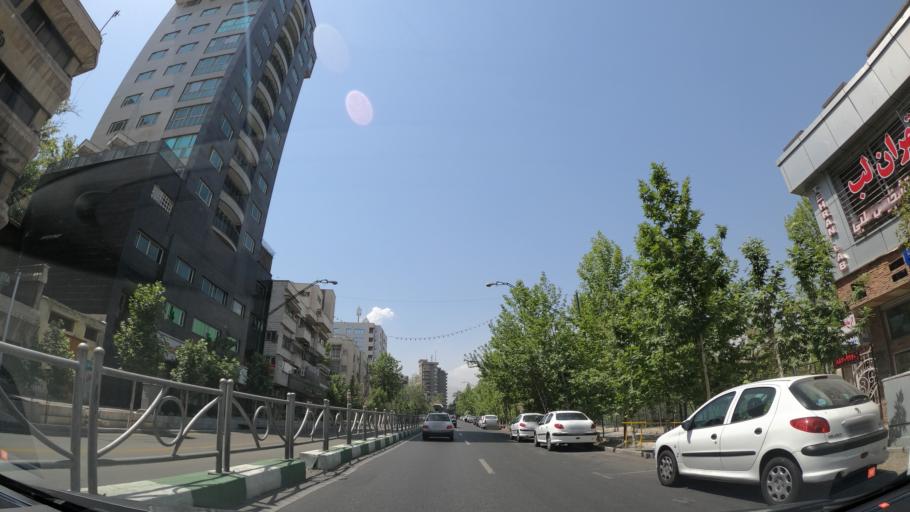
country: IR
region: Tehran
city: Tehran
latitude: 35.7341
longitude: 51.4104
